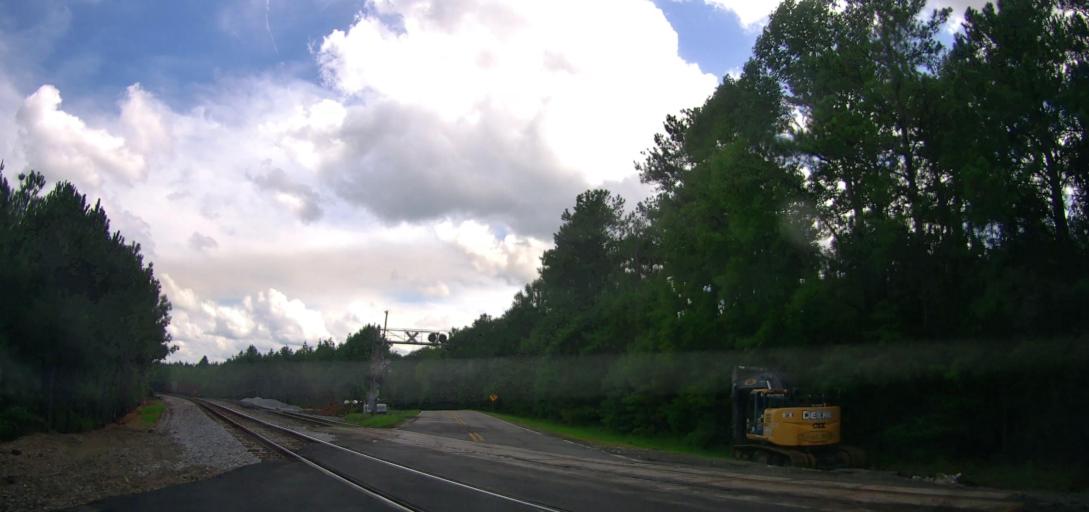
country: US
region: Georgia
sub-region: Talbot County
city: Talbotton
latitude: 32.6358
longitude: -84.4930
